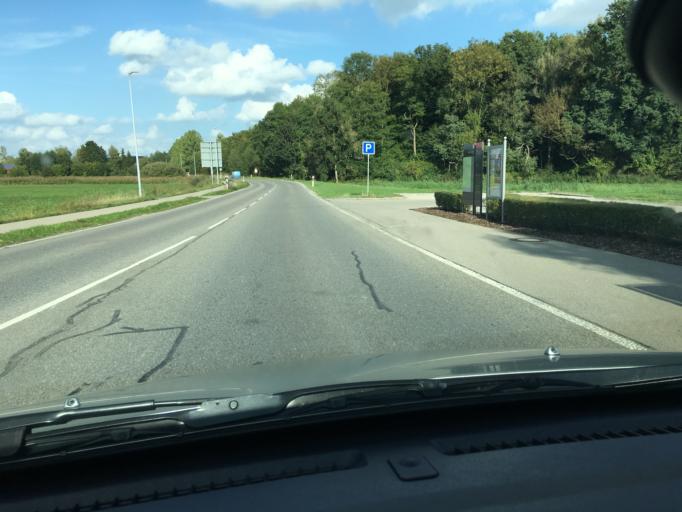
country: DE
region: Baden-Wuerttemberg
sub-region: Tuebingen Region
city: Bad Schussenried
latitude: 47.9981
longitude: 9.6634
